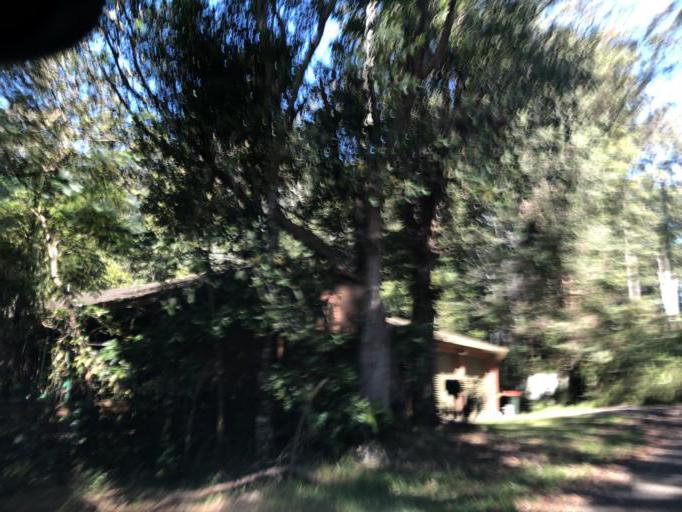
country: AU
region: New South Wales
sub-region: Bellingen
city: Bellingen
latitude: -30.4615
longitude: 152.8990
